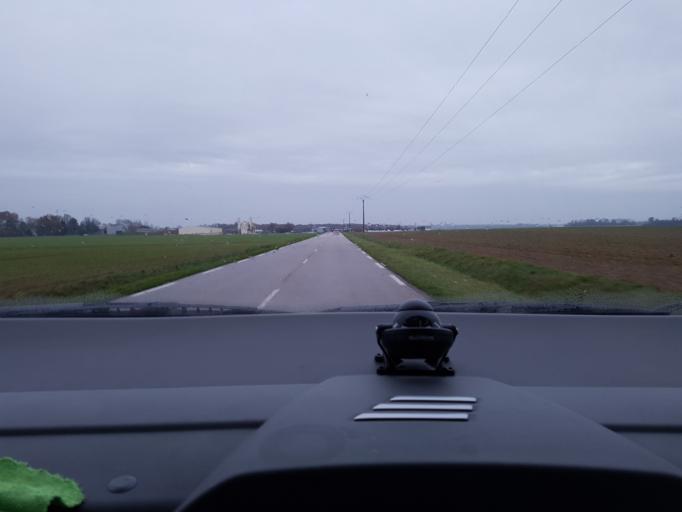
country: FR
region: Haute-Normandie
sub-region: Departement de l'Eure
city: Le Neubourg
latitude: 49.1463
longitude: 0.9518
